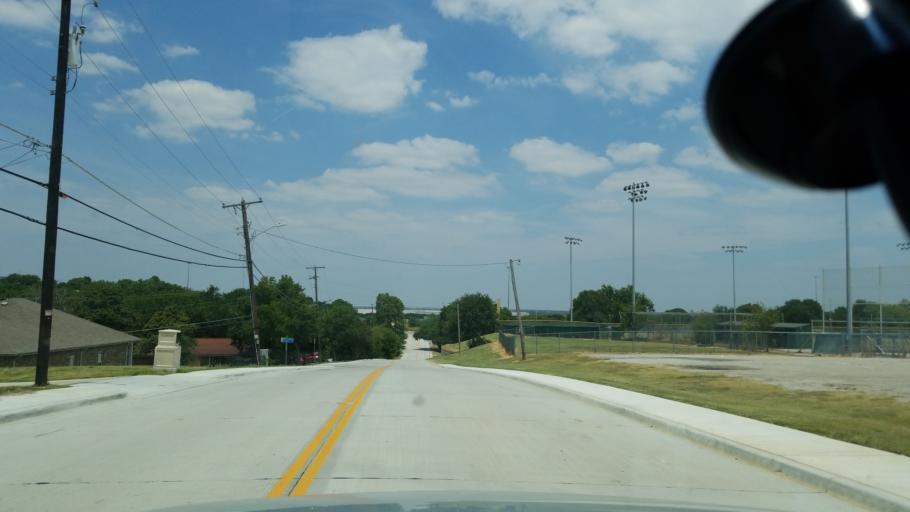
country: US
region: Texas
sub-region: Dallas County
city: Grand Prairie
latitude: 32.7526
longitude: -96.9982
